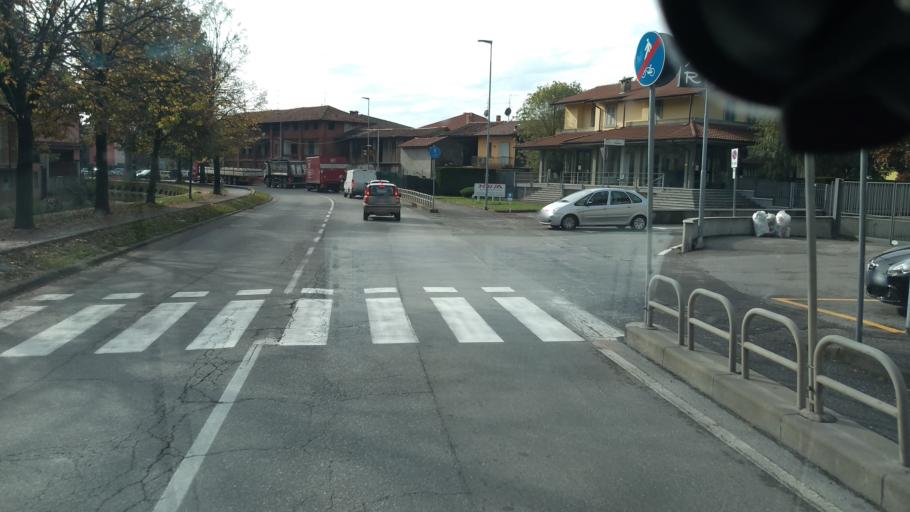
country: IT
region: Lombardy
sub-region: Provincia di Bergamo
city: Cologno al Serio
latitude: 45.5794
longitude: 9.7040
